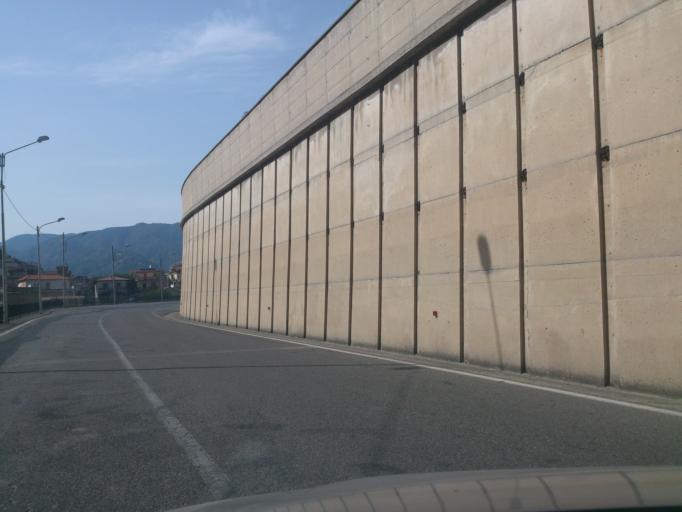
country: IT
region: Calabria
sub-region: Provincia di Reggio Calabria
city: Pazzano
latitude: 38.4737
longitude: 16.4548
